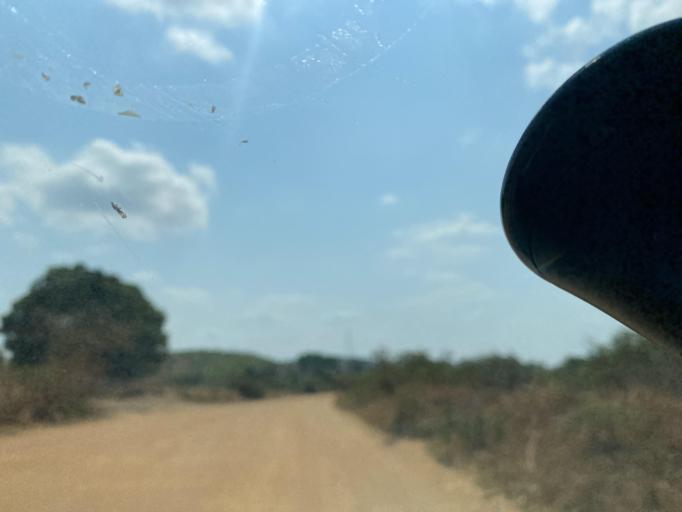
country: ZM
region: Lusaka
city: Chongwe
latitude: -15.6034
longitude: 28.7431
